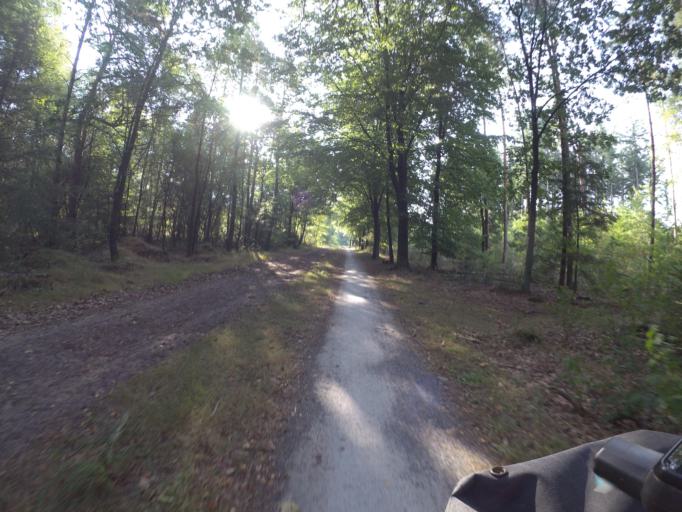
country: NL
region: Drenthe
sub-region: Gemeente Westerveld
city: Dwingeloo
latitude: 52.9213
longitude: 6.3292
